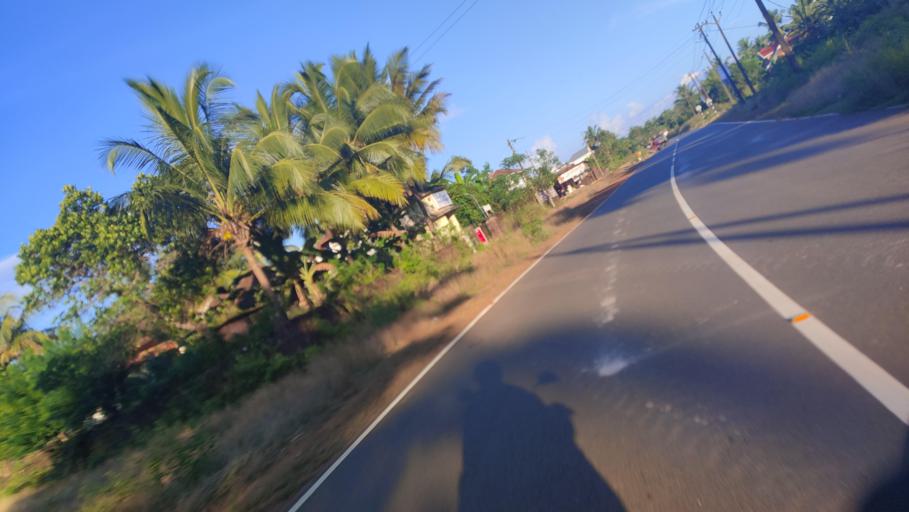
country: IN
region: Kerala
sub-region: Kasaragod District
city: Kasaragod
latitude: 12.4649
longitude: 75.0725
